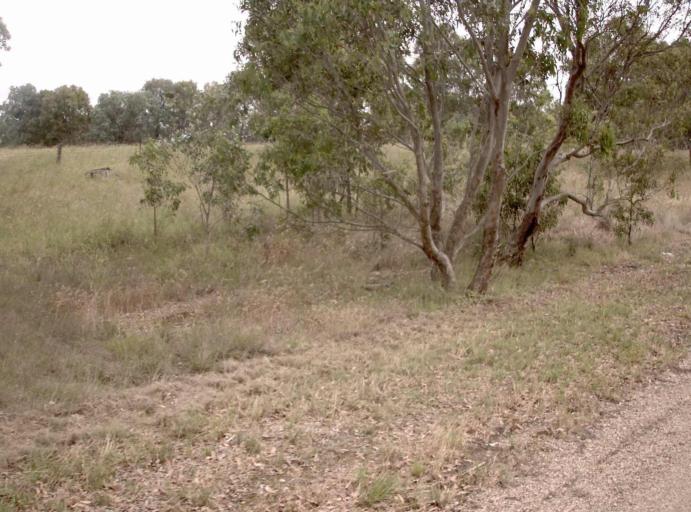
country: AU
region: Victoria
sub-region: Wellington
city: Sale
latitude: -37.9406
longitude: 147.0930
